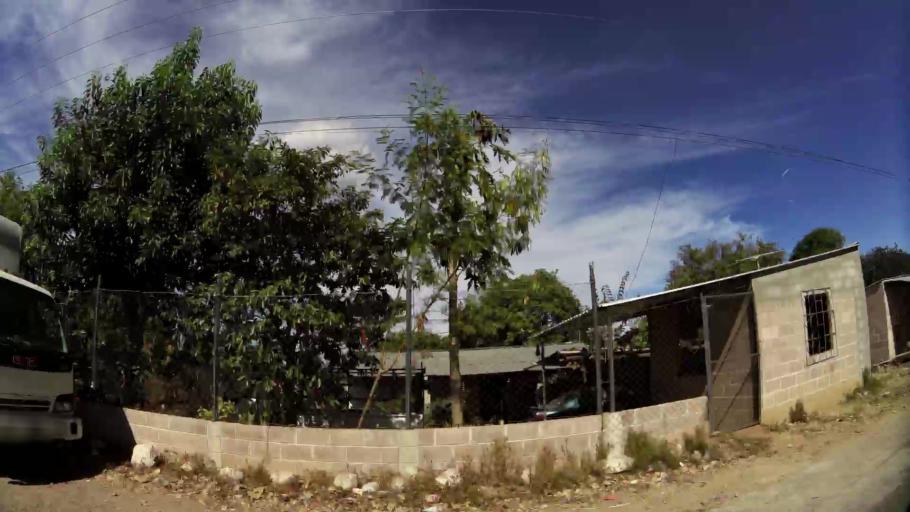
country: SV
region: San Salvador
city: Aguilares
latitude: 13.9604
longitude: -89.1077
